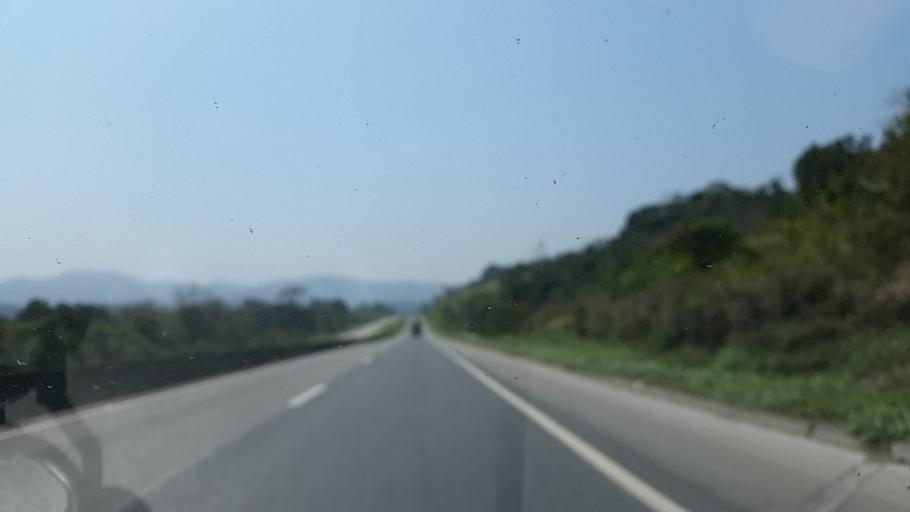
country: BR
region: Sao Paulo
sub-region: Miracatu
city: Miracatu
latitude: -24.1804
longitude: -47.3513
